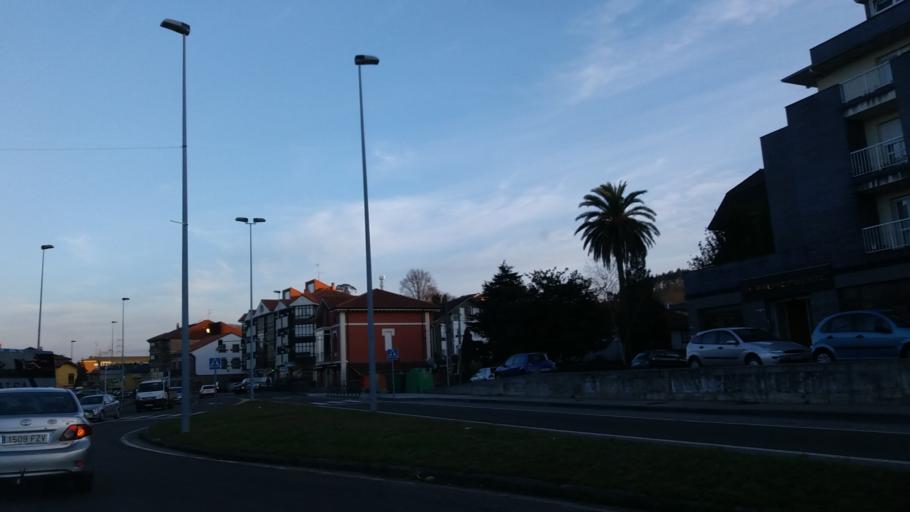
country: ES
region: Cantabria
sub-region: Provincia de Cantabria
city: Reocin
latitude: 43.3584
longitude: -4.0890
